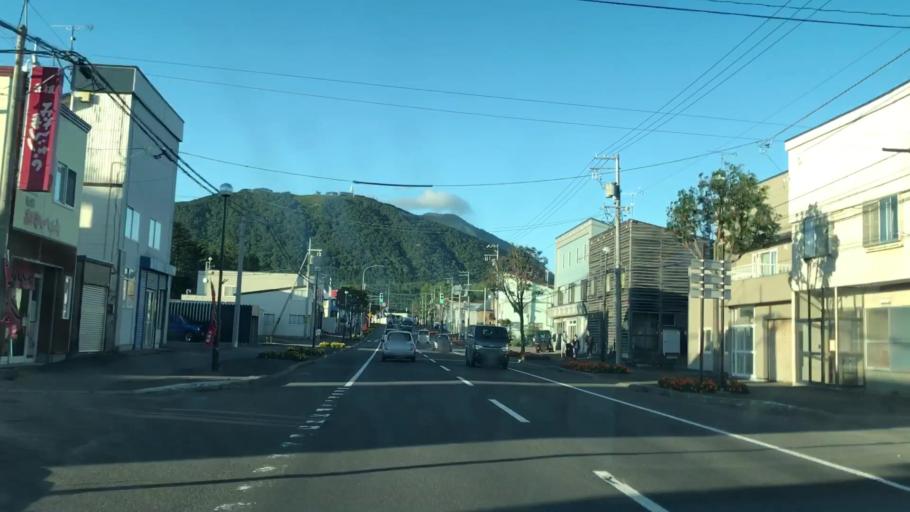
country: JP
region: Hokkaido
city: Niseko Town
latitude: 42.7348
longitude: 140.8745
